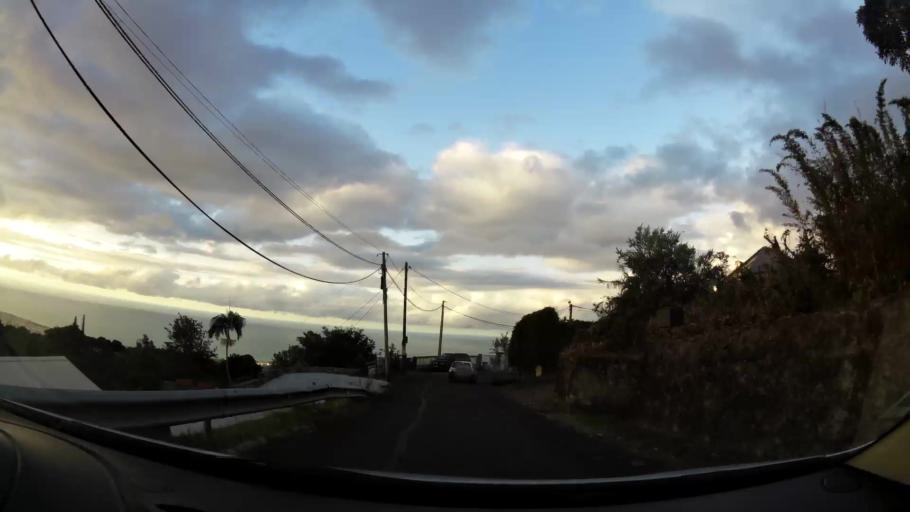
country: RE
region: Reunion
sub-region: Reunion
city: Saint-Denis
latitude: -20.9179
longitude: 55.4635
